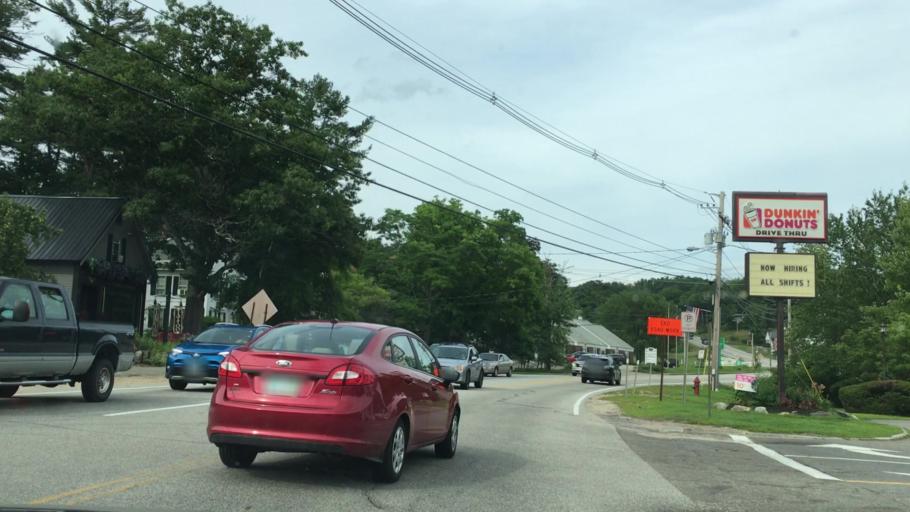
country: US
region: New Hampshire
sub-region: Belknap County
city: Meredith
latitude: 43.6607
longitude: -71.4962
